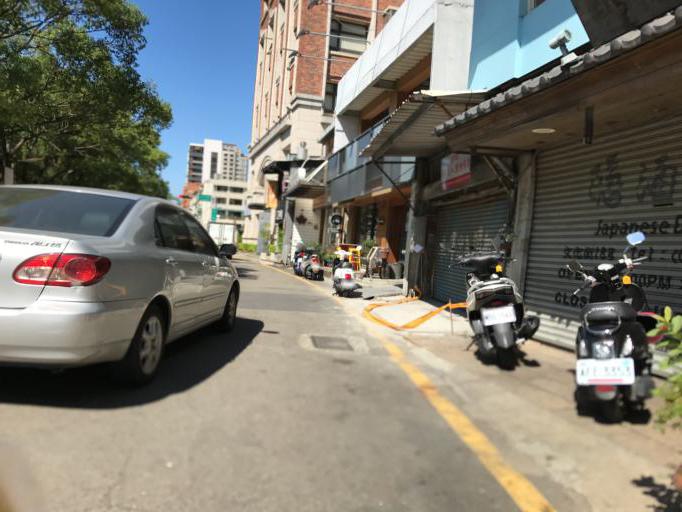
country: TW
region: Taiwan
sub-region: Hsinchu
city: Hsinchu
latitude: 24.8064
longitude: 120.9711
